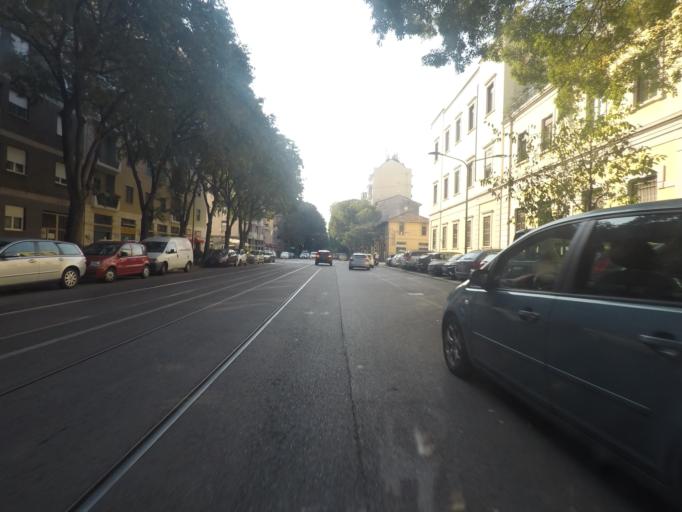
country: IT
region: Lombardy
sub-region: Citta metropolitana di Milano
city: Sesto San Giovanni
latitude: 45.4896
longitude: 9.2298
